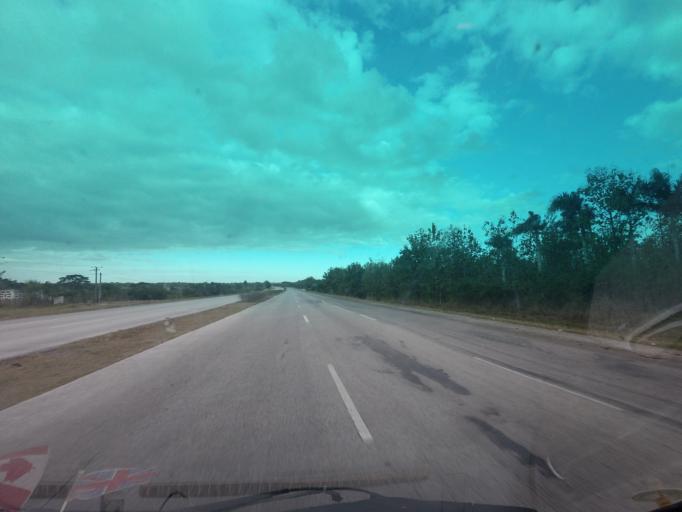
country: CU
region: Villa Clara
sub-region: Municipio de Ranchuelo
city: Ranchuelo
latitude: 22.4045
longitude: -80.1652
